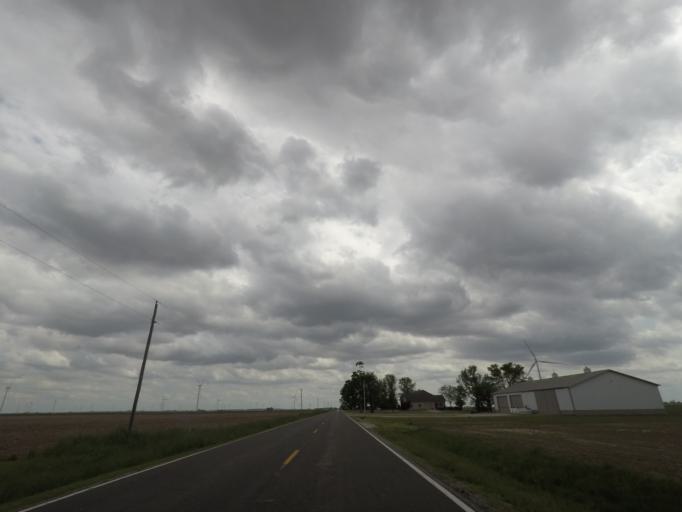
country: US
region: Illinois
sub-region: Macon County
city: Warrensburg
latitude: 40.0244
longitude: -89.0855
